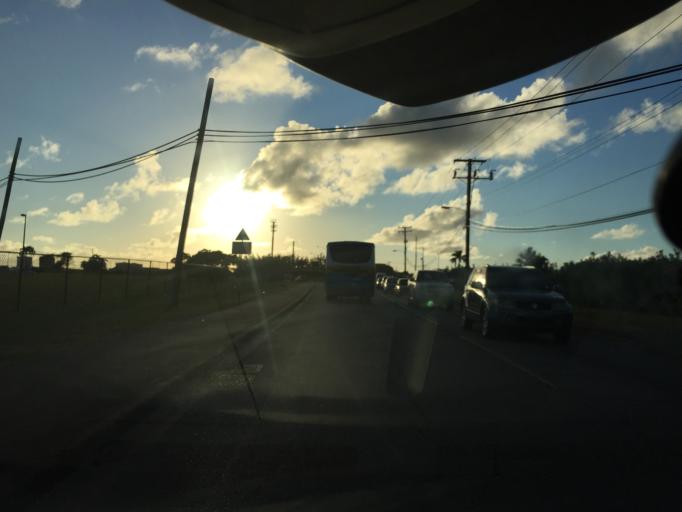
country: BB
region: Saint Philip
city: Crane
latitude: 13.0810
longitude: -59.4896
